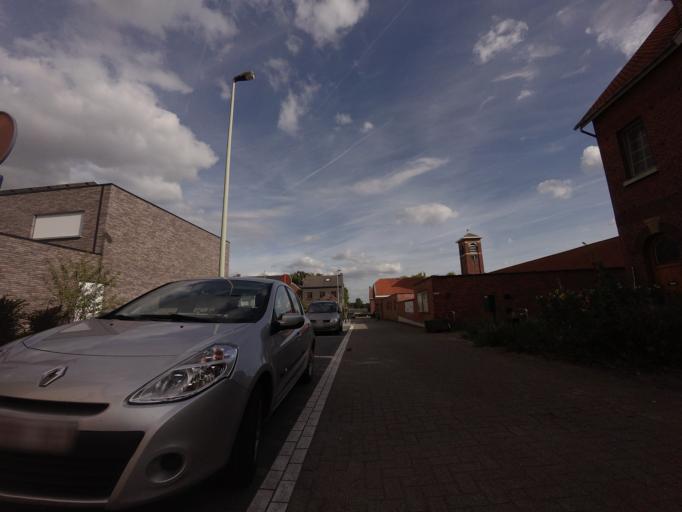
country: BE
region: Flanders
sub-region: Provincie Antwerpen
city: Rumst
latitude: 51.0870
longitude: 4.4566
